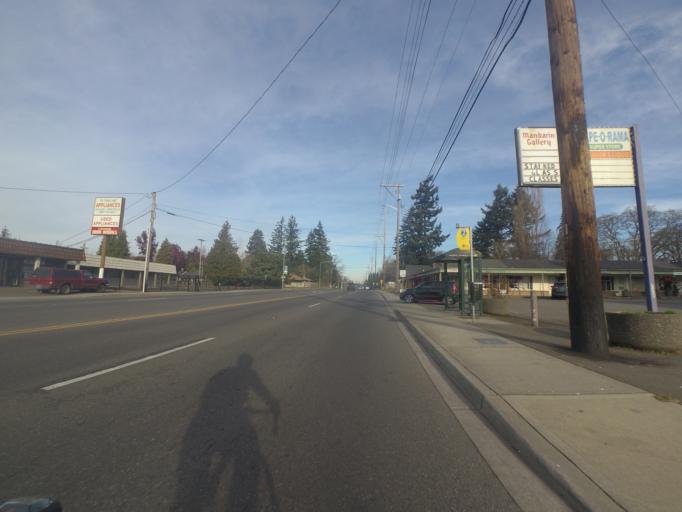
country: US
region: Washington
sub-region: Pierce County
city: Lakewood
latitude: 47.1770
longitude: -122.5180
